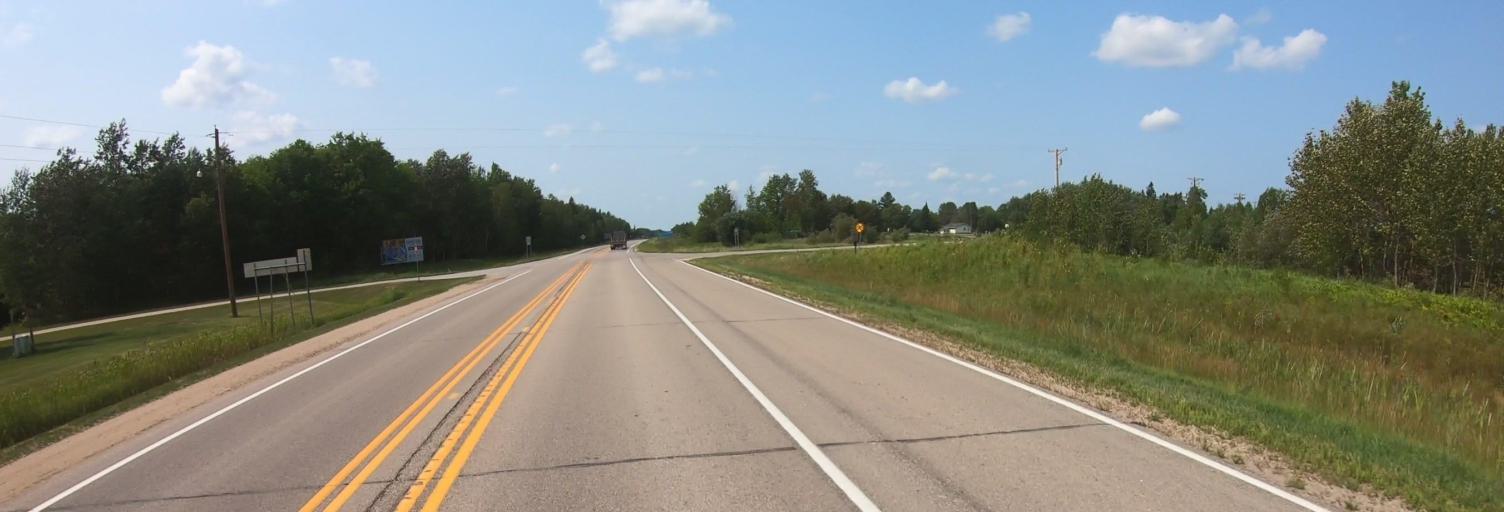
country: US
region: Minnesota
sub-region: Roseau County
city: Warroad
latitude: 48.7990
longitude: -95.0898
